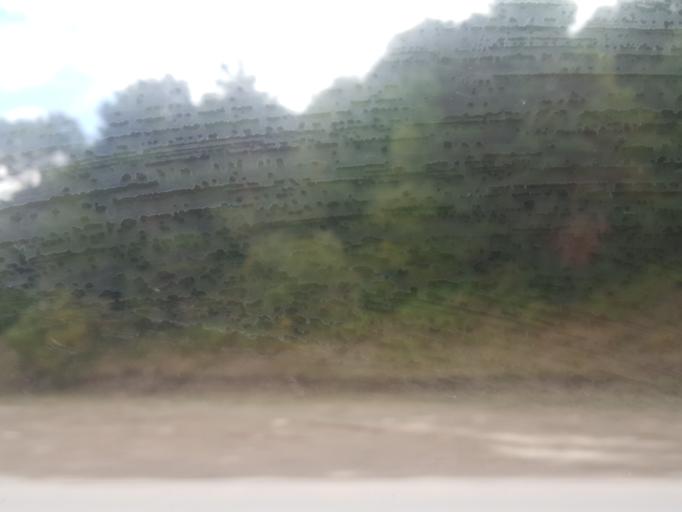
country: TR
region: Tokat
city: Bereketli
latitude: 40.5412
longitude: 37.3078
